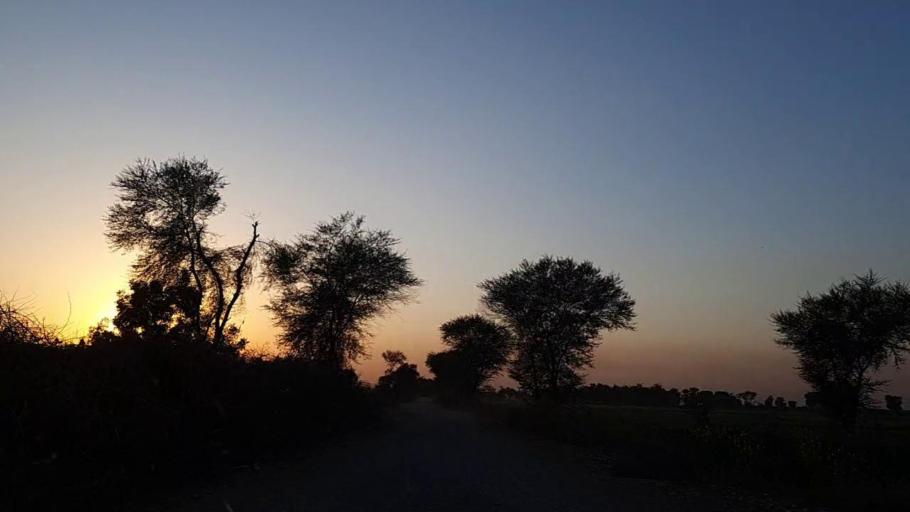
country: PK
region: Sindh
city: Daur
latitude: 26.3504
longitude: 68.3139
